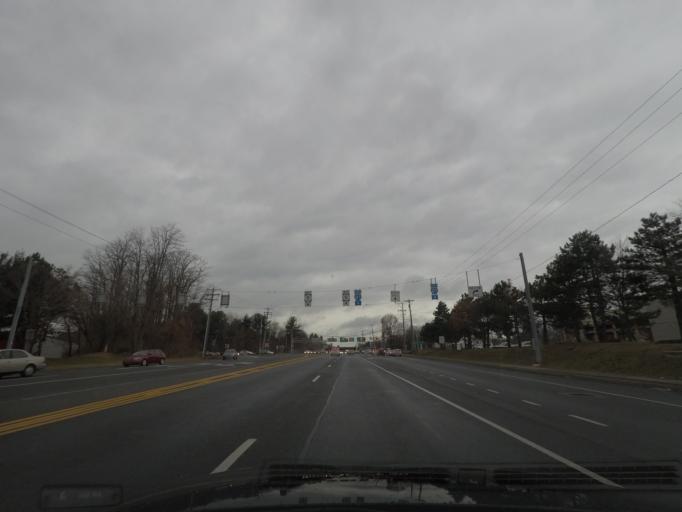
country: US
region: New York
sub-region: Albany County
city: Colonie
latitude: 42.7077
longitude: -73.8214
